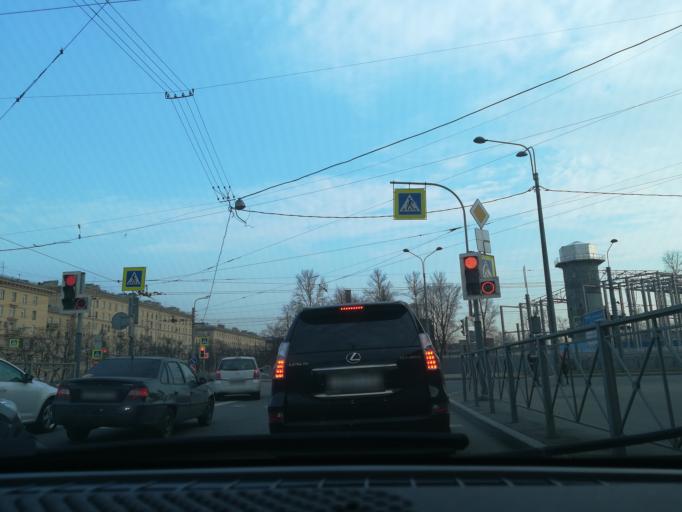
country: RU
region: St.-Petersburg
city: Avtovo
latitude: 59.8731
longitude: 30.2545
